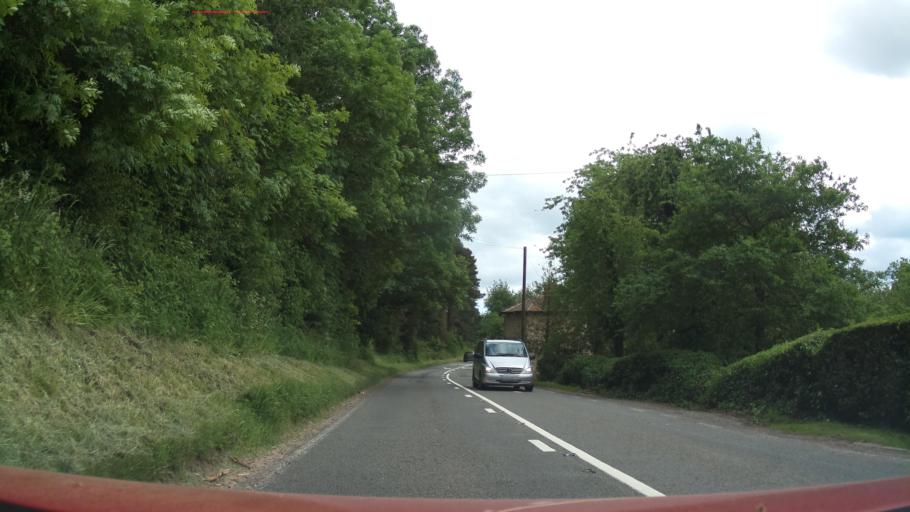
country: GB
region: England
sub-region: Herefordshire
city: Yatton
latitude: 51.9537
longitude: -2.5314
